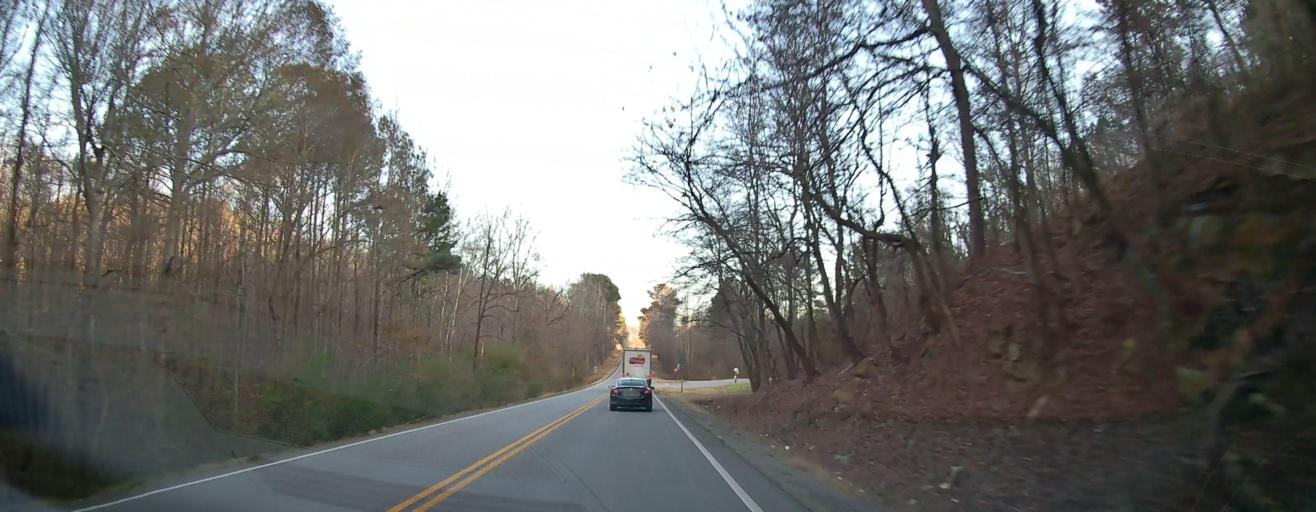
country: US
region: Alabama
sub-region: Blount County
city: Oneonta
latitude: 34.0787
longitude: -86.3378
